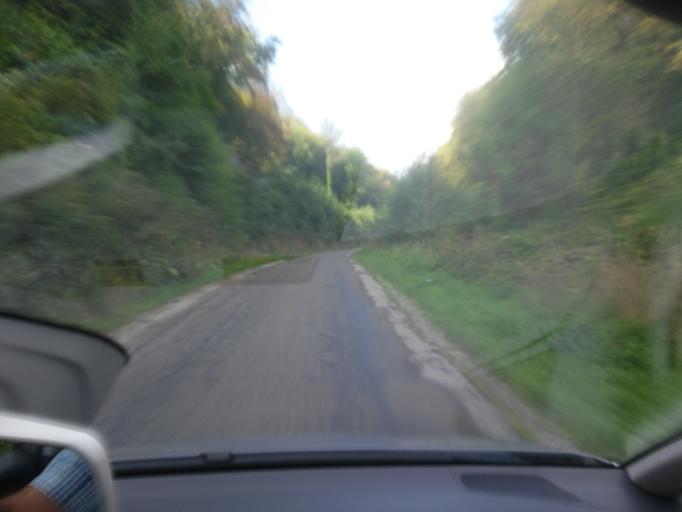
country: FR
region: Lorraine
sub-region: Departement de la Meuse
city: Montmedy
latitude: 49.4949
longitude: 5.4232
